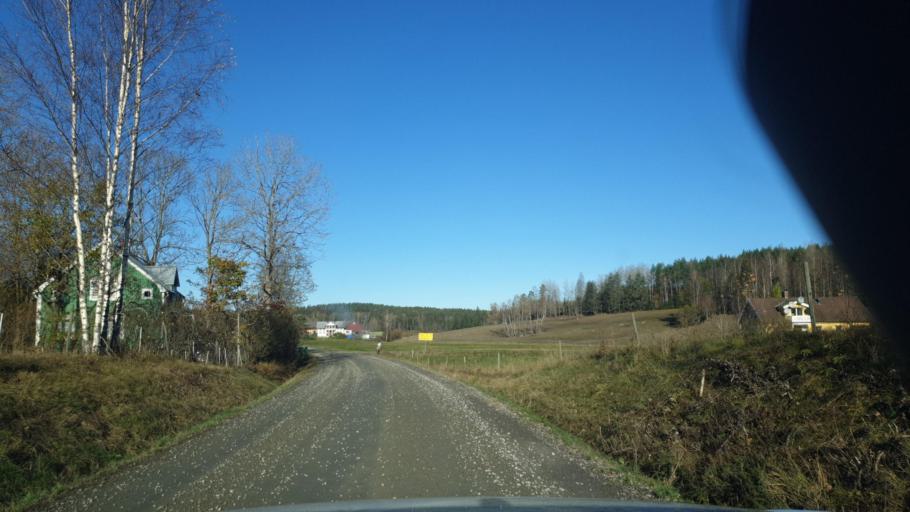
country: SE
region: Vaermland
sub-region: Karlstads Kommun
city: Edsvalla
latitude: 59.5026
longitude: 13.0309
